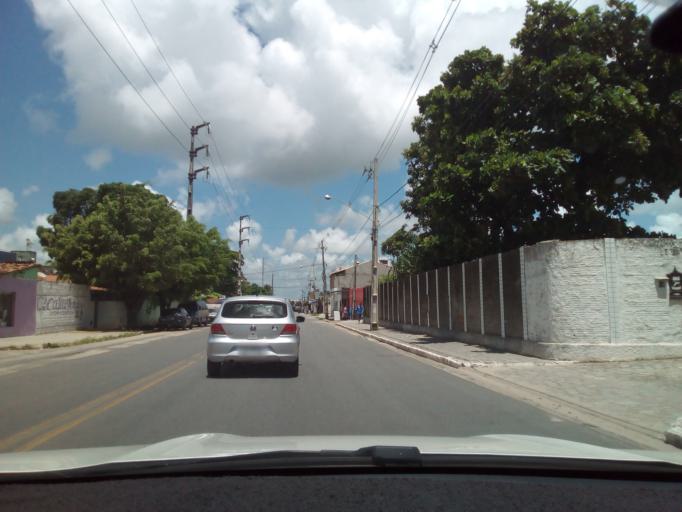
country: BR
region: Paraiba
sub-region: Joao Pessoa
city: Joao Pessoa
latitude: -7.1828
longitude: -34.8737
